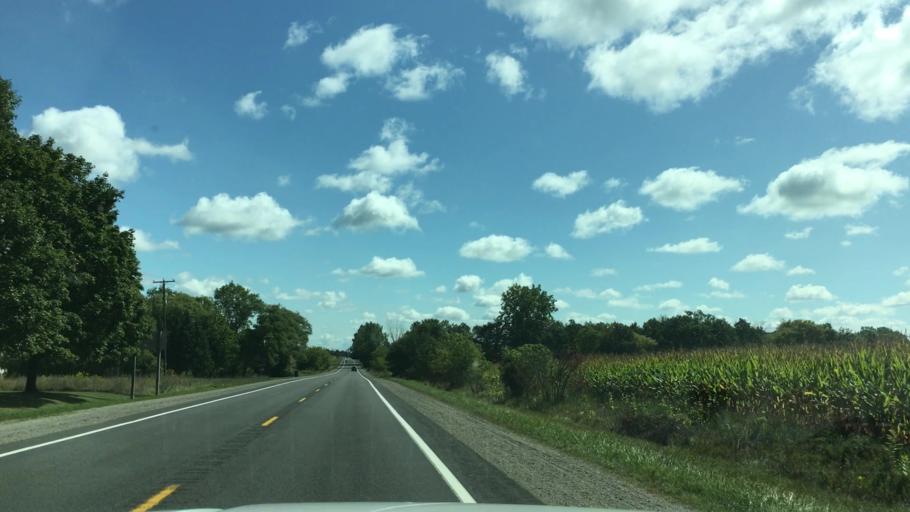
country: US
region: Michigan
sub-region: Montcalm County
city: Carson City
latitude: 43.1774
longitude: -84.9133
